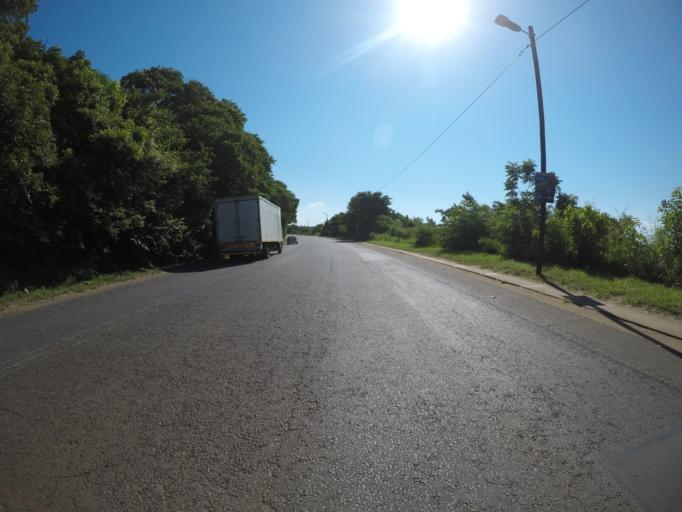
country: ZA
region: KwaZulu-Natal
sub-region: uThungulu District Municipality
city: Empangeni
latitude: -28.7756
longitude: 31.8882
